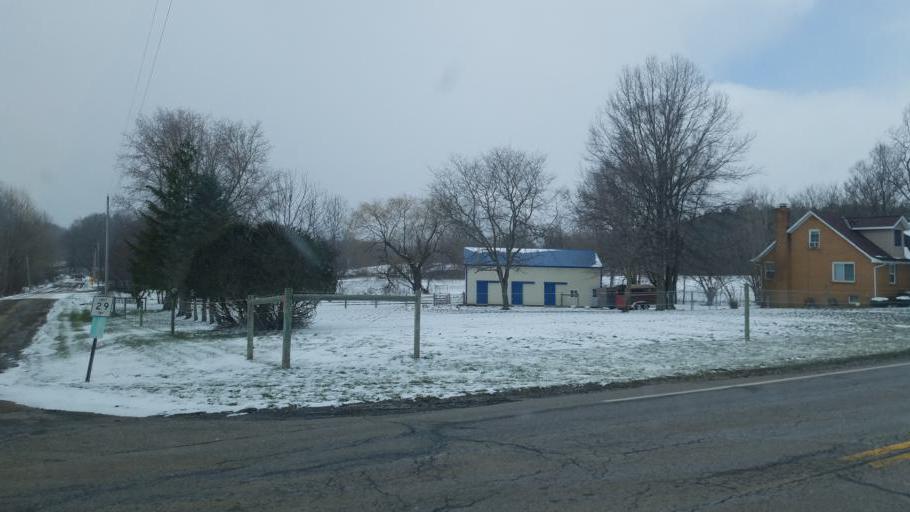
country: US
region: Ohio
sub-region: Richland County
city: Lexington
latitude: 40.6372
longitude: -82.6632
